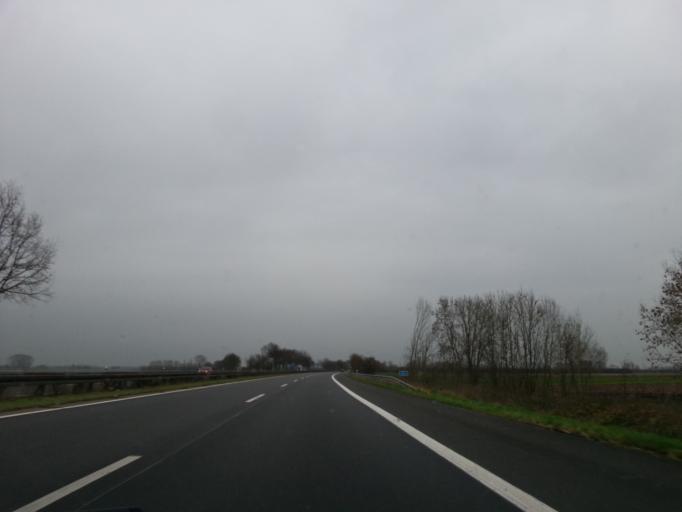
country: NL
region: Gelderland
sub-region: Oude IJsselstreek
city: Gendringen
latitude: 51.8432
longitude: 6.3386
